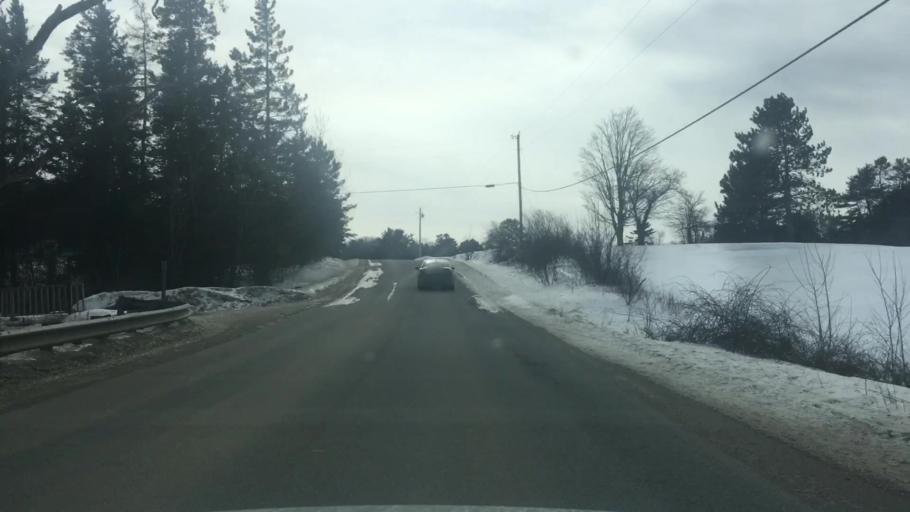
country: US
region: Maine
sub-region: Hancock County
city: Orland
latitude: 44.5931
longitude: -68.7248
